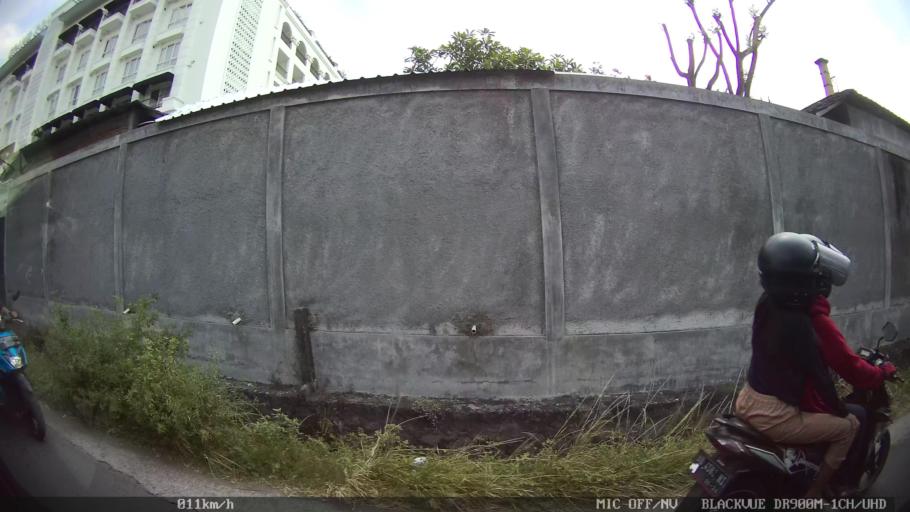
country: ID
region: Daerah Istimewa Yogyakarta
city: Depok
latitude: -7.7977
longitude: 110.4056
